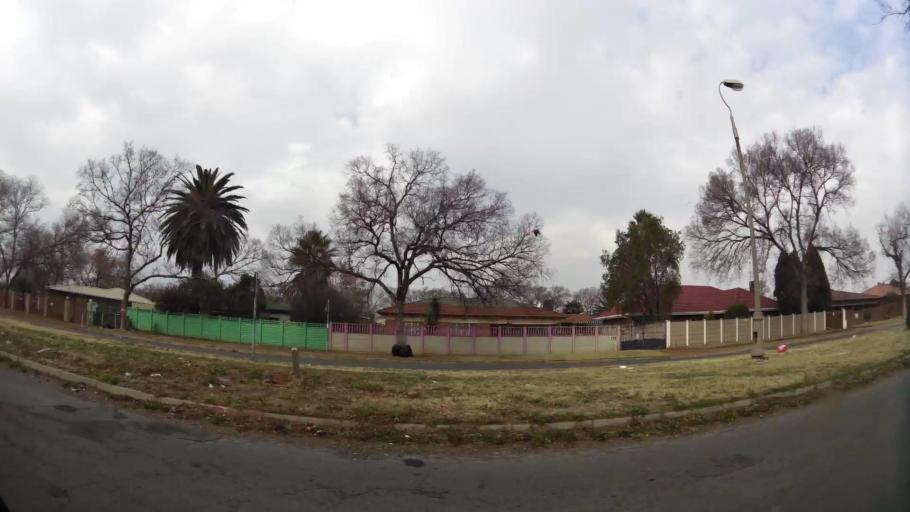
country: ZA
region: Gauteng
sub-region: Sedibeng District Municipality
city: Vanderbijlpark
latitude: -26.6842
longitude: 27.8315
